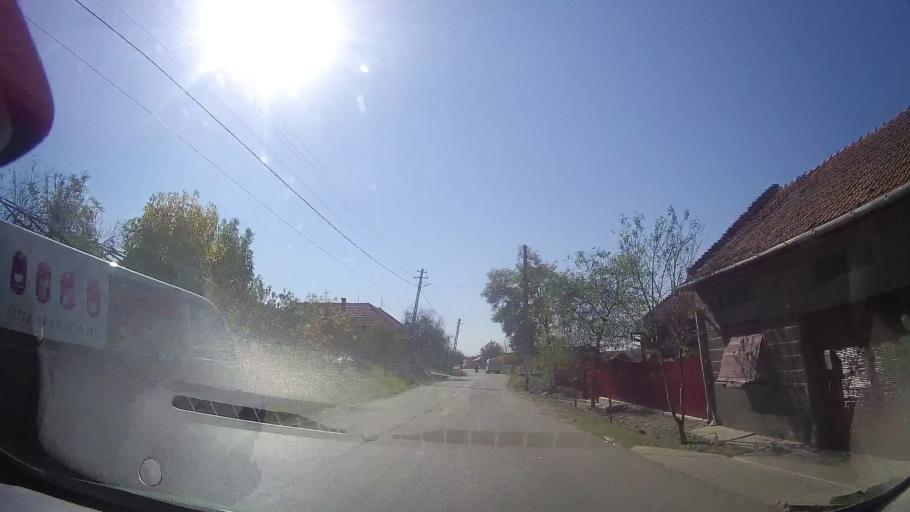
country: RO
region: Timis
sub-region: Comuna Bethausen
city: Bethausen
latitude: 45.8587
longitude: 21.9684
